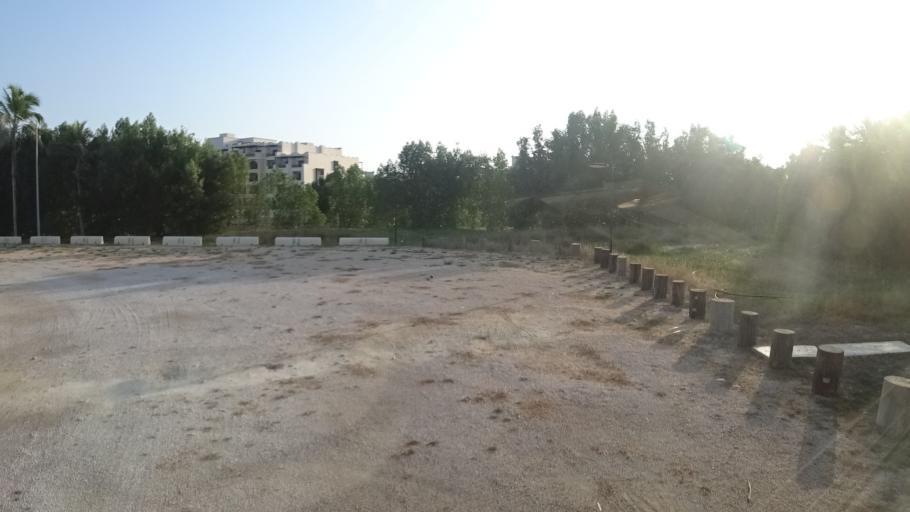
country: OM
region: Zufar
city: Salalah
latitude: 17.0343
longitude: 54.3024
